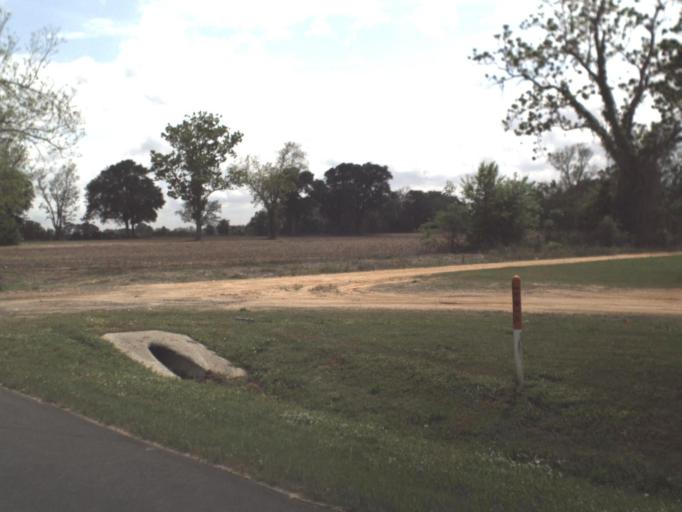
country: US
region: Florida
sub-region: Escambia County
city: Century
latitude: 30.9358
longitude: -87.1569
